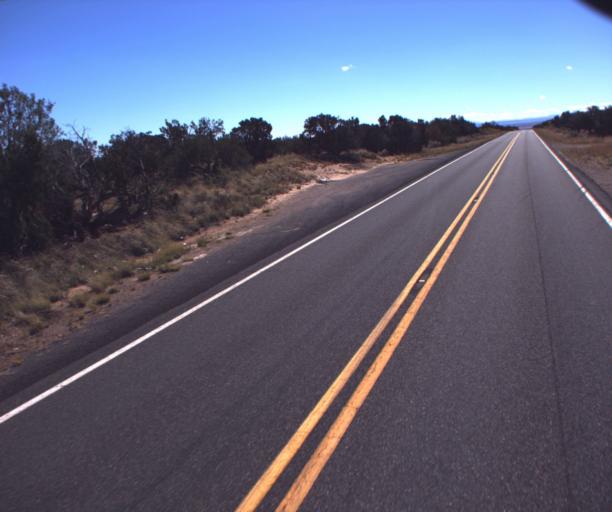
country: US
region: Arizona
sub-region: Apache County
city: Saint Johns
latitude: 34.8421
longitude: -109.2376
